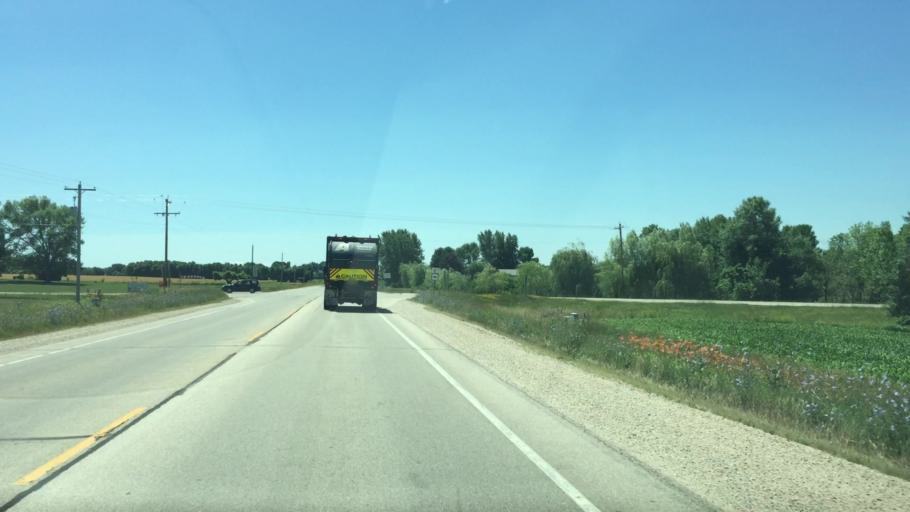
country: US
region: Wisconsin
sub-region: Calumet County
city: Chilton
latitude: 44.0739
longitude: -88.1634
